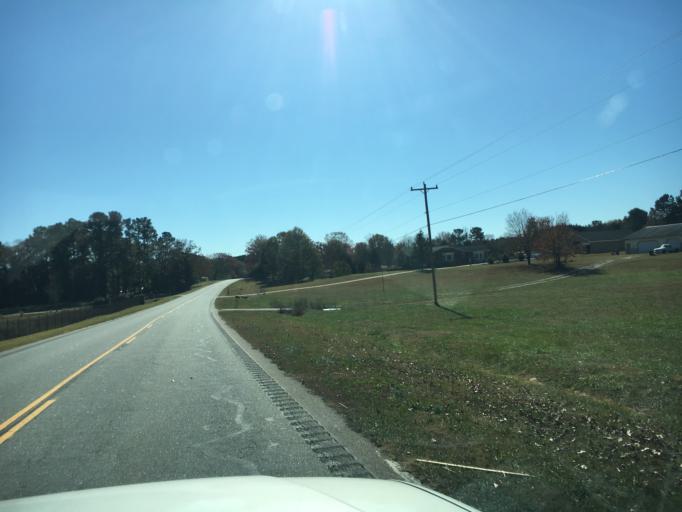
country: US
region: South Carolina
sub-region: Anderson County
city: Centerville
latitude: 34.4710
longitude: -82.7870
